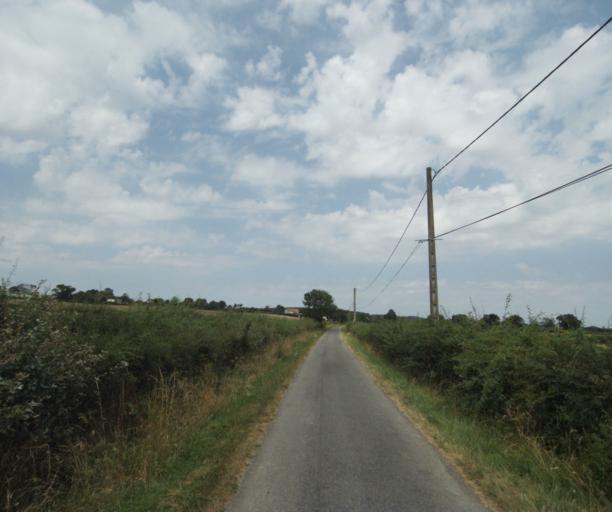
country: FR
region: Bourgogne
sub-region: Departement de Saone-et-Loire
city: Gueugnon
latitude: 46.5855
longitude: 4.0414
